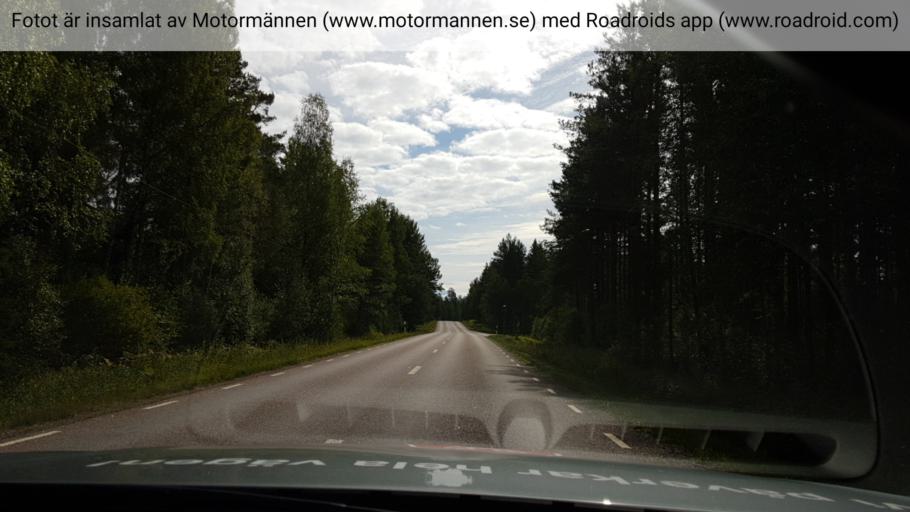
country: SE
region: Uppsala
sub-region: Heby Kommun
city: OEstervala
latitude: 60.0371
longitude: 17.2522
